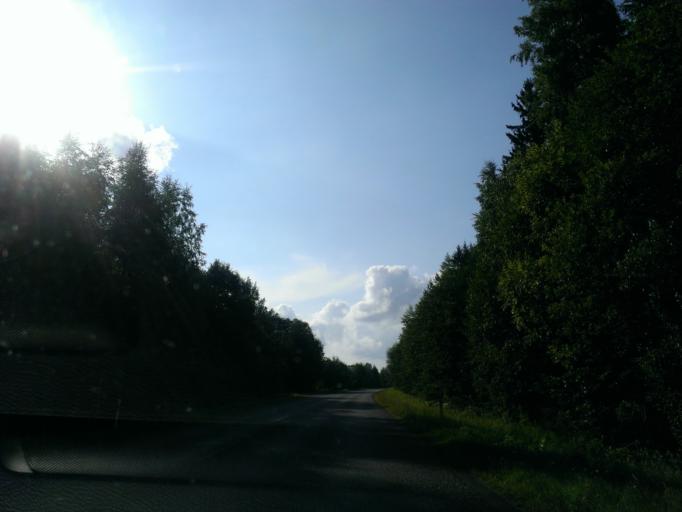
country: LV
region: Priekuli
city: Priekuli
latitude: 57.2948
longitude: 25.4279
